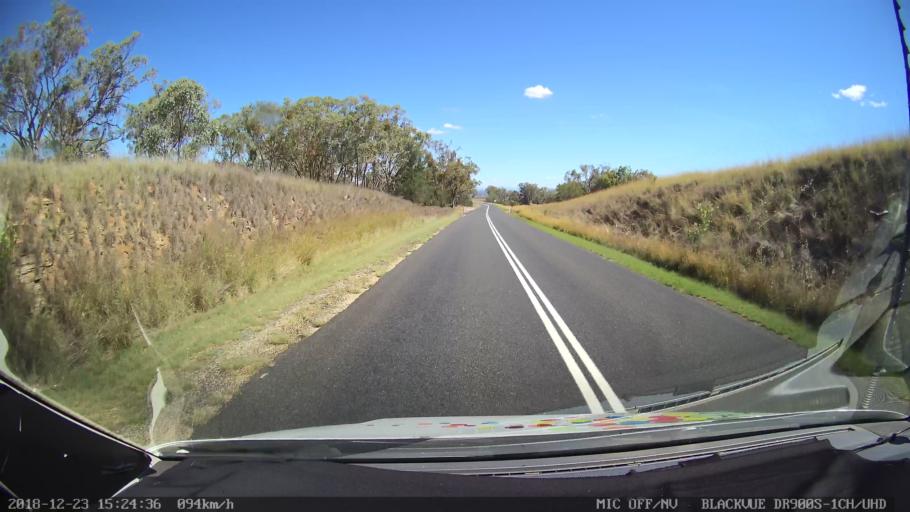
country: AU
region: New South Wales
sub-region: Tamworth Municipality
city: Manilla
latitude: -30.8938
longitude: 150.8242
